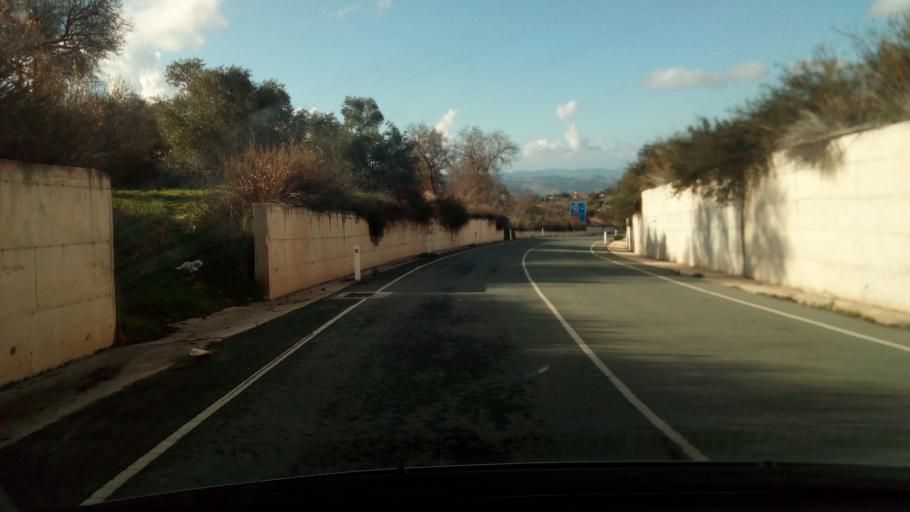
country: CY
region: Pafos
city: Tala
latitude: 34.9322
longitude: 32.5181
